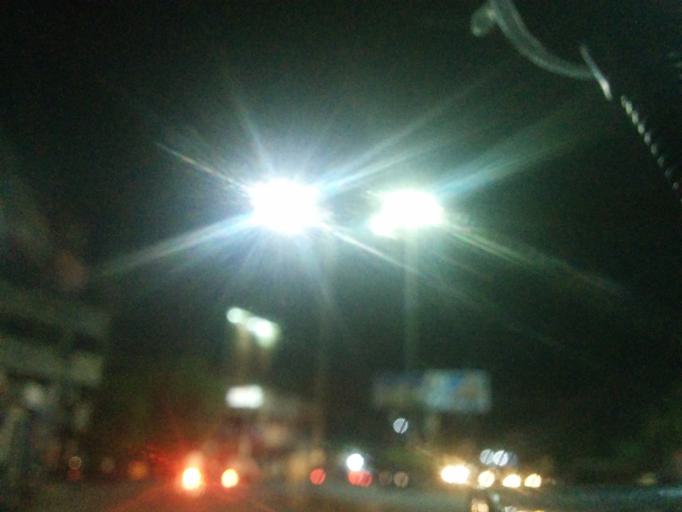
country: IN
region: Andhra Pradesh
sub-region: East Godavari
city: Rajahmundry
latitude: 17.0093
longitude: 81.7800
